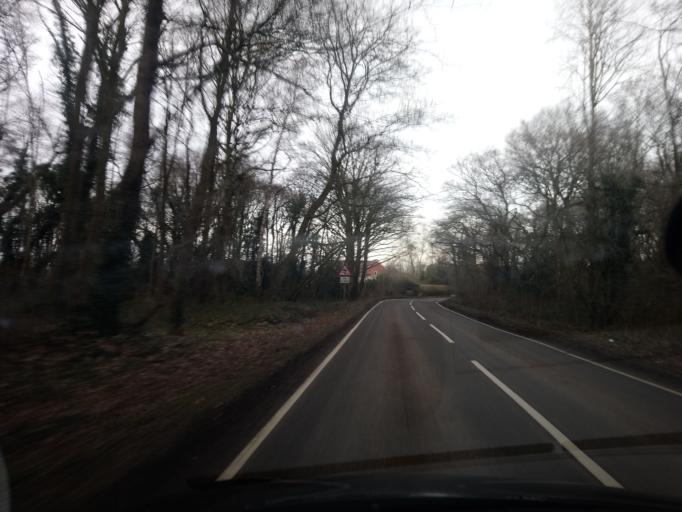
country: GB
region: England
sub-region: Shropshire
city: Prees
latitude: 52.9236
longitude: -2.6808
